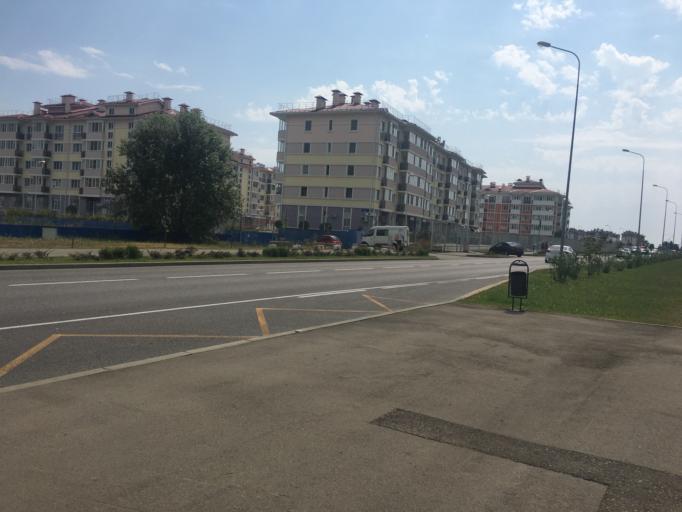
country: RU
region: Krasnodarskiy
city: Adler
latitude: 43.4031
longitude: 39.9791
